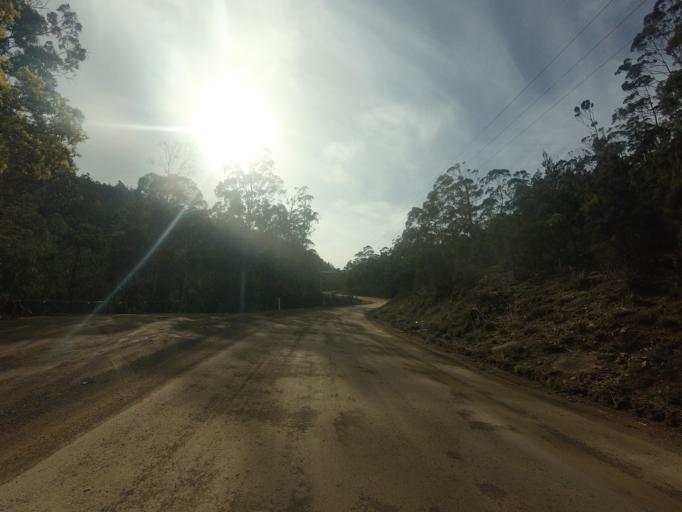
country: AU
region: Tasmania
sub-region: Huon Valley
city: Huonville
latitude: -43.0562
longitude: 147.0986
